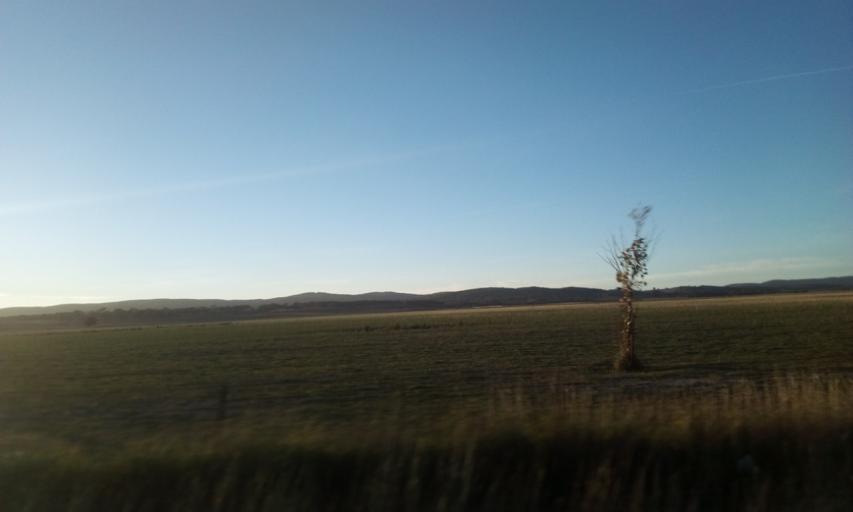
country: AU
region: New South Wales
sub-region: Goulburn Mulwaree
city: Goulburn
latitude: -34.8454
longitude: 149.5585
